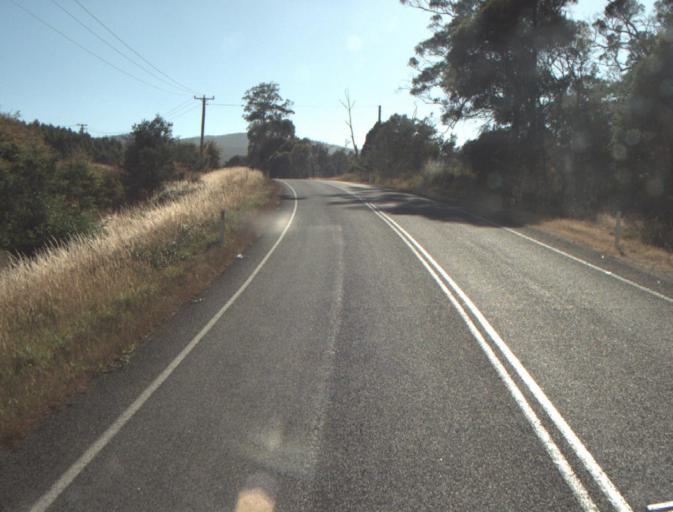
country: AU
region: Tasmania
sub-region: Launceston
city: Newstead
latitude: -41.4189
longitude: 147.2778
